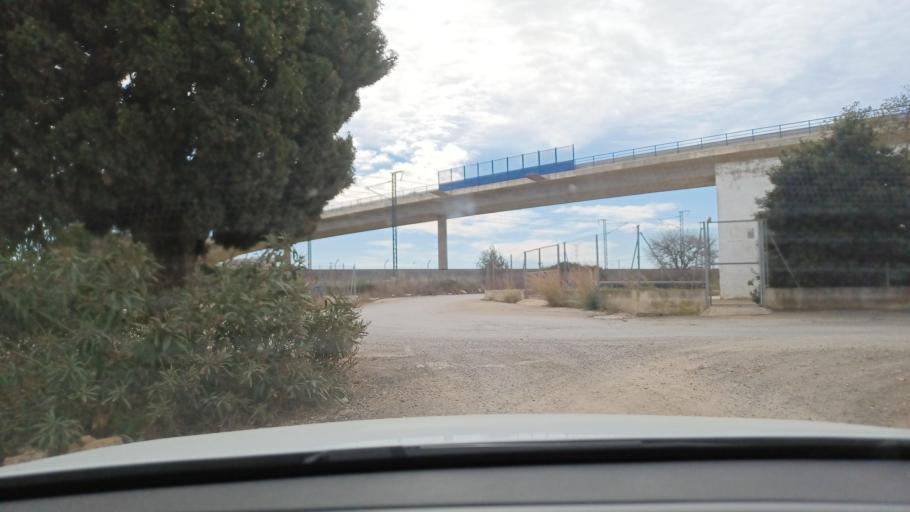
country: ES
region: Valencia
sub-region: Provincia de Valencia
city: Benifaio
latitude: 39.2888
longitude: -0.4395
